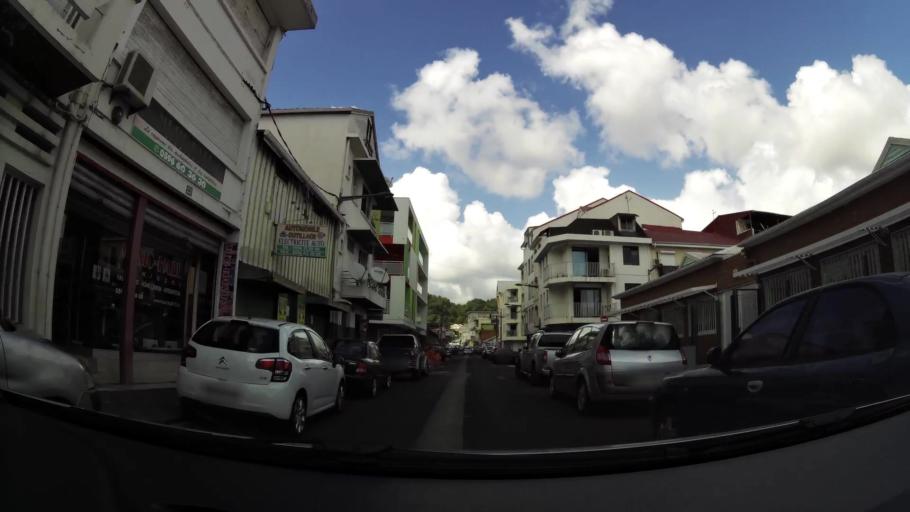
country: MQ
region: Martinique
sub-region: Martinique
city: Fort-de-France
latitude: 14.6114
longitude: -61.0723
